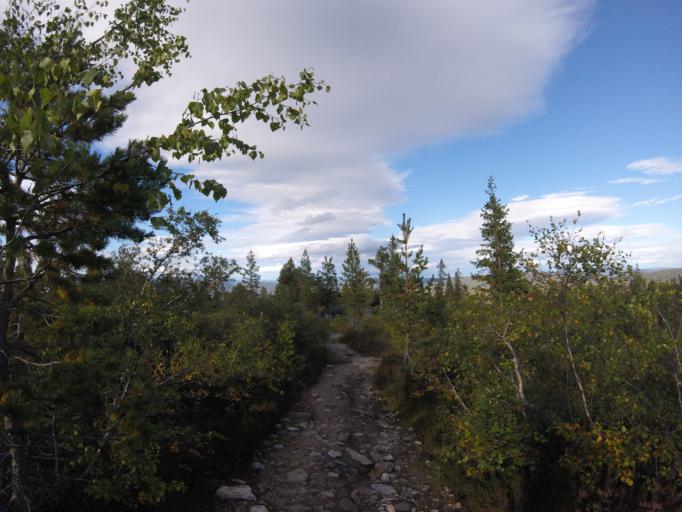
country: NO
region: Buskerud
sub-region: Flesberg
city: Lampeland
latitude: 59.7853
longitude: 9.4153
